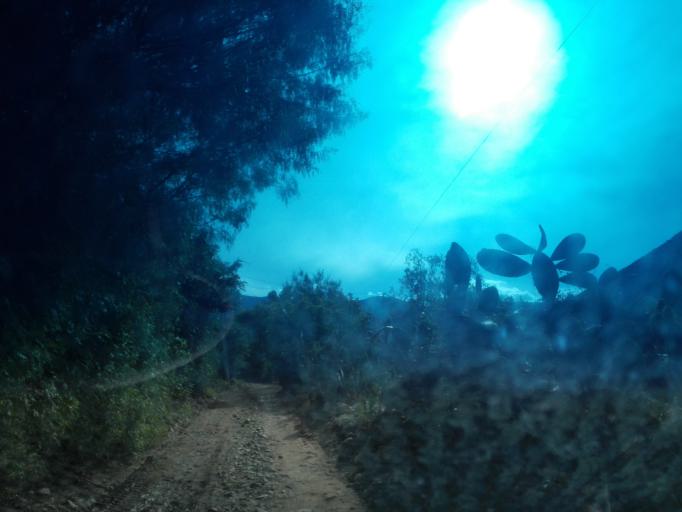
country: PE
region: Ayacucho
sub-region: Provincia de Huamanga
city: Pacaycasa
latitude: -13.0681
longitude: -74.2493
